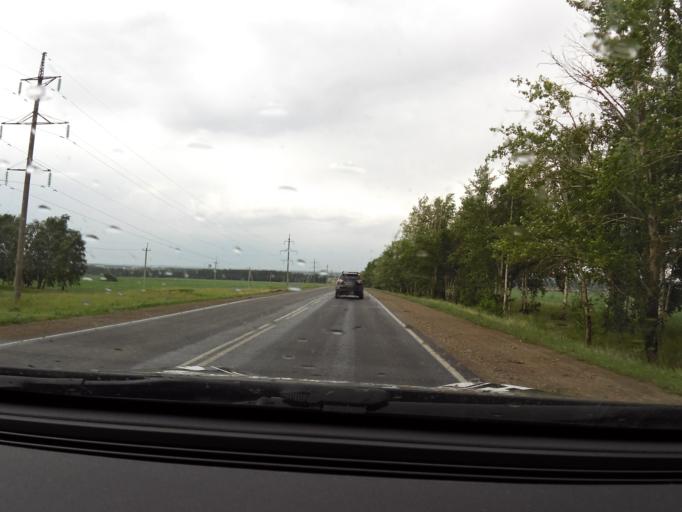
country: RU
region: Bashkortostan
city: Mikhaylovka
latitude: 54.8551
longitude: 55.7659
